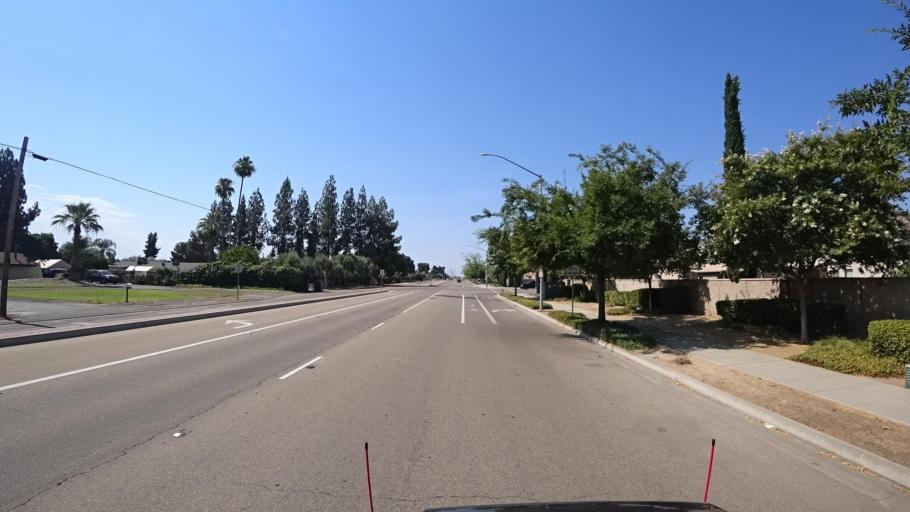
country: US
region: California
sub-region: Fresno County
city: Sunnyside
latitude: 36.7209
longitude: -119.6822
